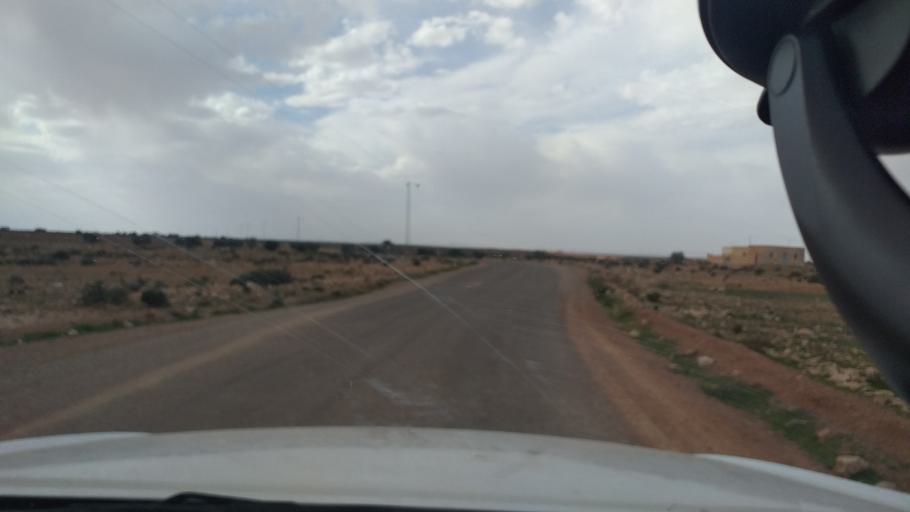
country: TN
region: Madanin
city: Medenine
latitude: 33.2901
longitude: 10.6057
